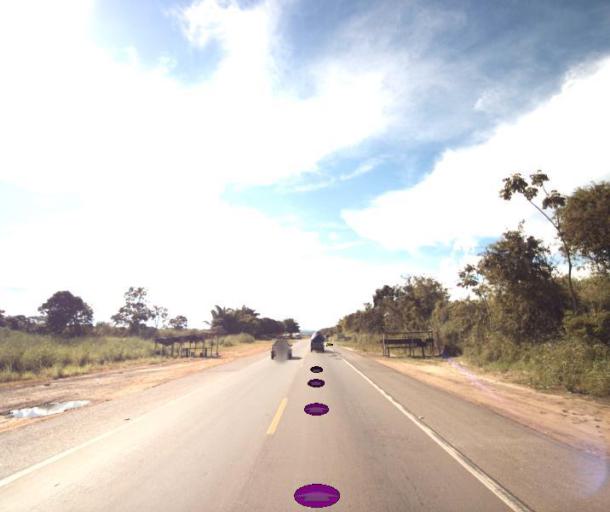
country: BR
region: Goias
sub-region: Rialma
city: Rialma
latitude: -15.4838
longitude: -49.4925
